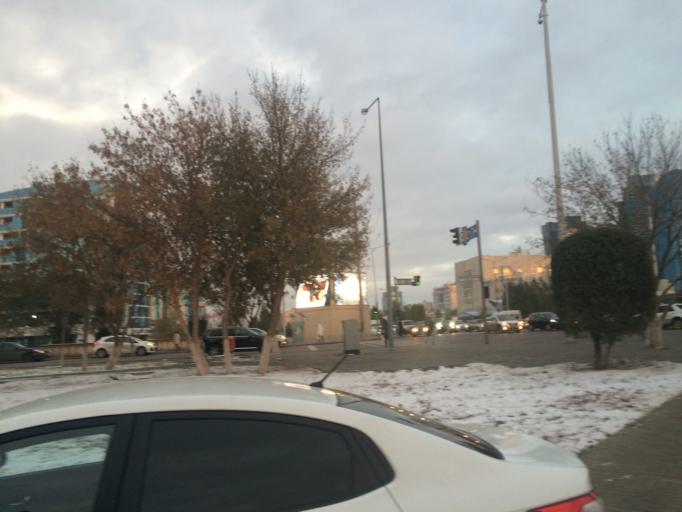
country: KZ
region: Astana Qalasy
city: Astana
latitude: 51.1369
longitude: 71.4153
